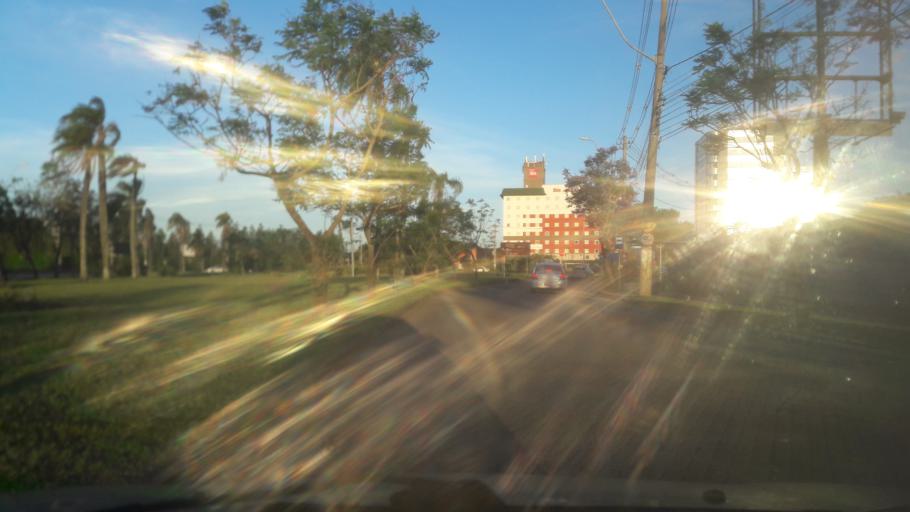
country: BR
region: Rio Grande do Sul
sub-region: Canoas
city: Canoas
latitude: -29.9880
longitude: -51.1727
